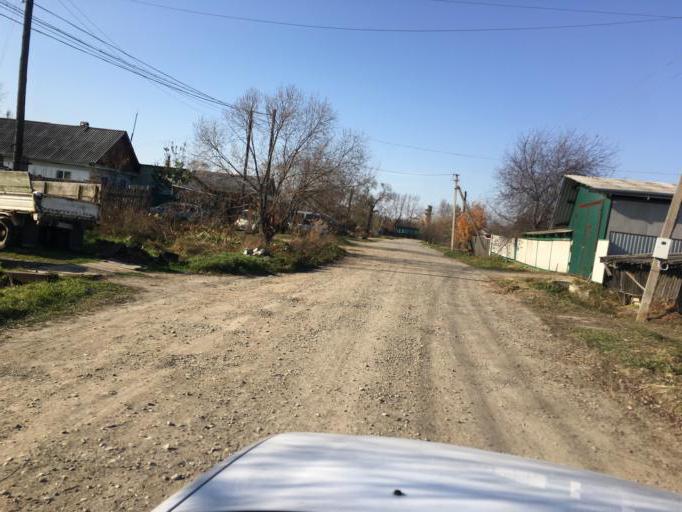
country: RU
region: Primorskiy
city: Dal'nerechensk
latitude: 45.9201
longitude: 133.7217
